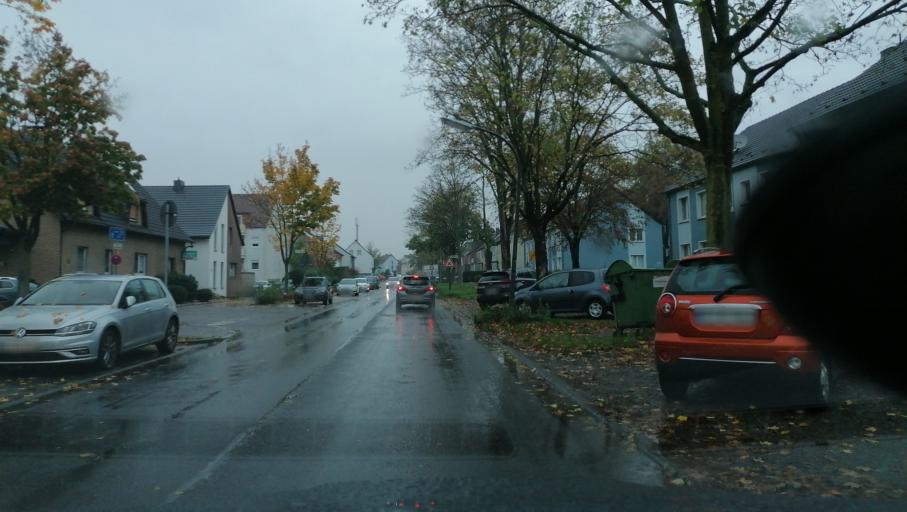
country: DE
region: North Rhine-Westphalia
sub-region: Regierungsbezirk Munster
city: Recklinghausen
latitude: 51.6031
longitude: 7.1799
